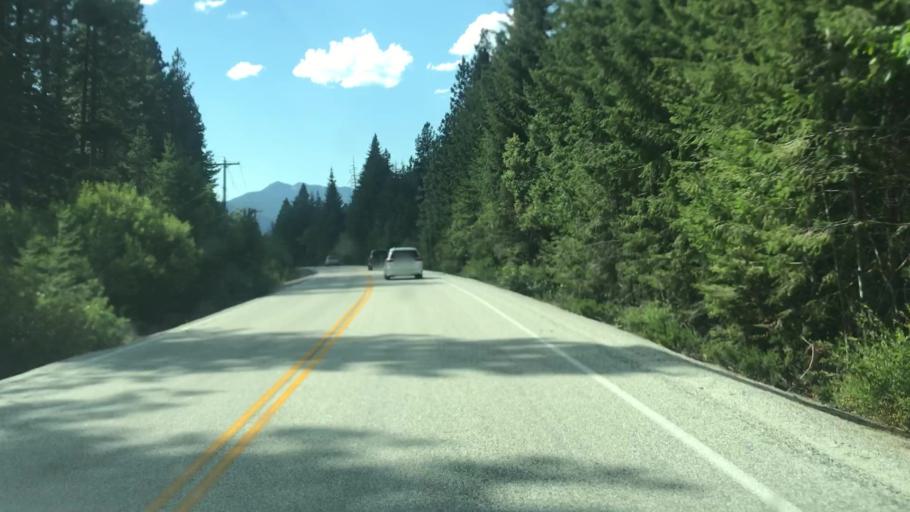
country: US
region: Washington
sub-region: Chelan County
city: Leavenworth
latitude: 47.8272
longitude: -120.7620
